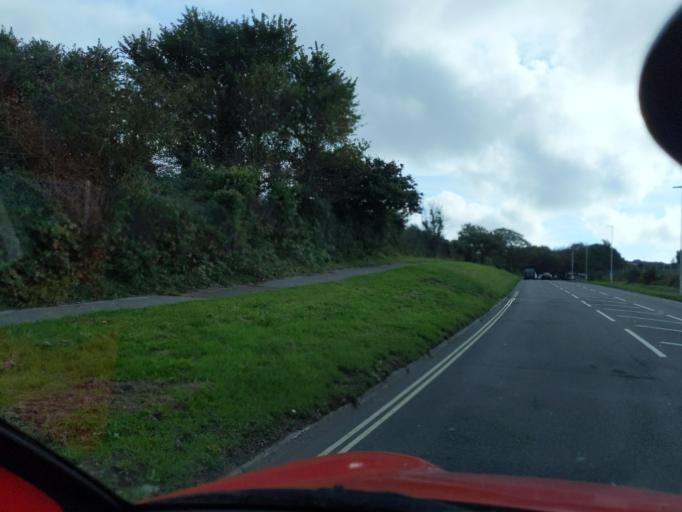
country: GB
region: England
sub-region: Cornwall
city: Saltash
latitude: 50.4160
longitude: -4.1861
